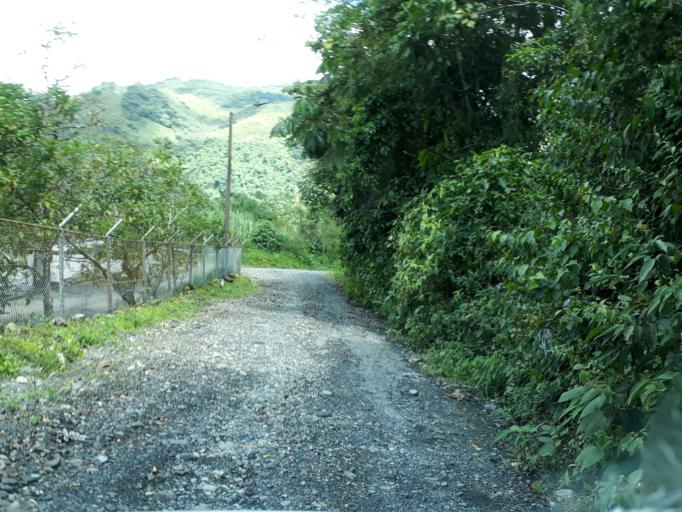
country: CO
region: Boyaca
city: Chivor
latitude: 4.7335
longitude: -73.3533
